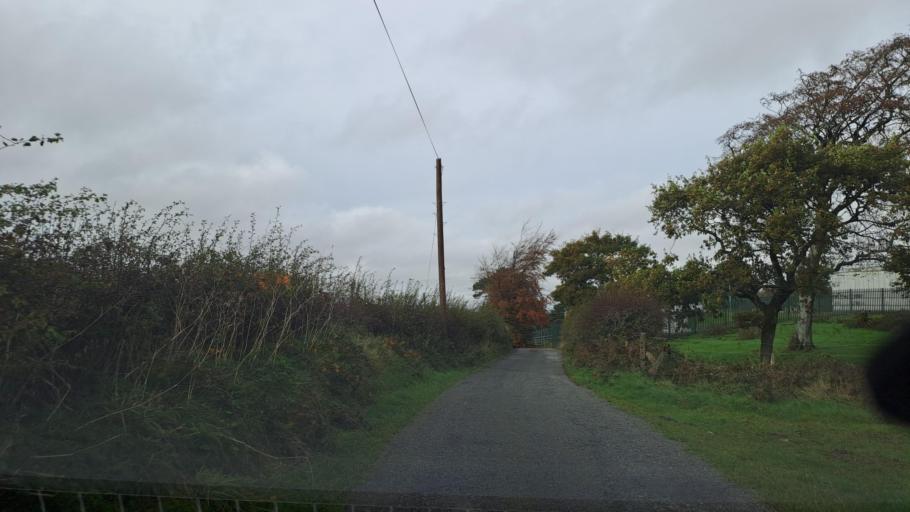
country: IE
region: Ulster
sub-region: County Monaghan
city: Carrickmacross
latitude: 54.0165
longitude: -6.8130
